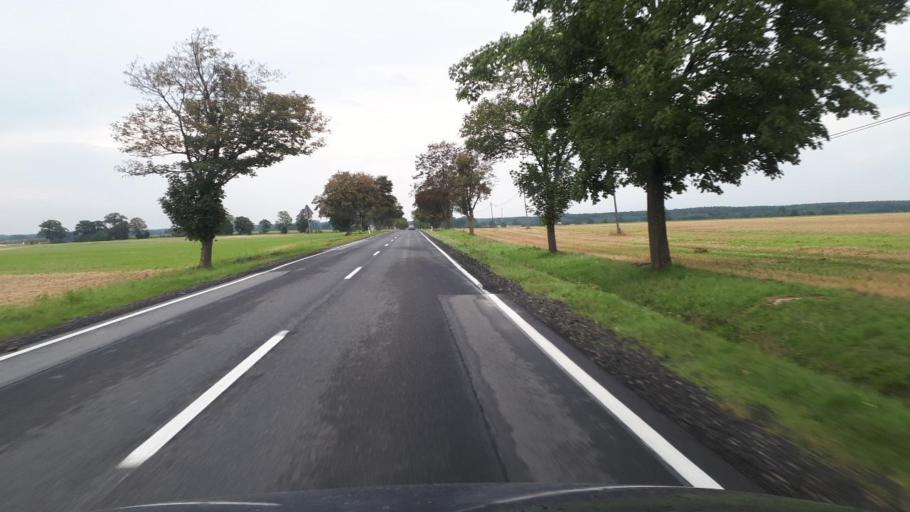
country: PL
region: Silesian Voivodeship
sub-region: Powiat lubliniecki
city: Sierakow Slaski
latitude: 50.8347
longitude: 18.5137
